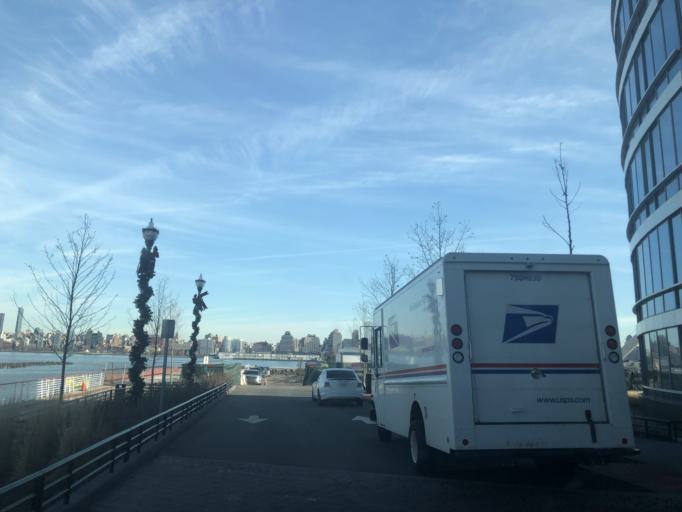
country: US
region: New Jersey
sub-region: Hudson County
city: Hoboken
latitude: 40.7311
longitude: -74.0301
